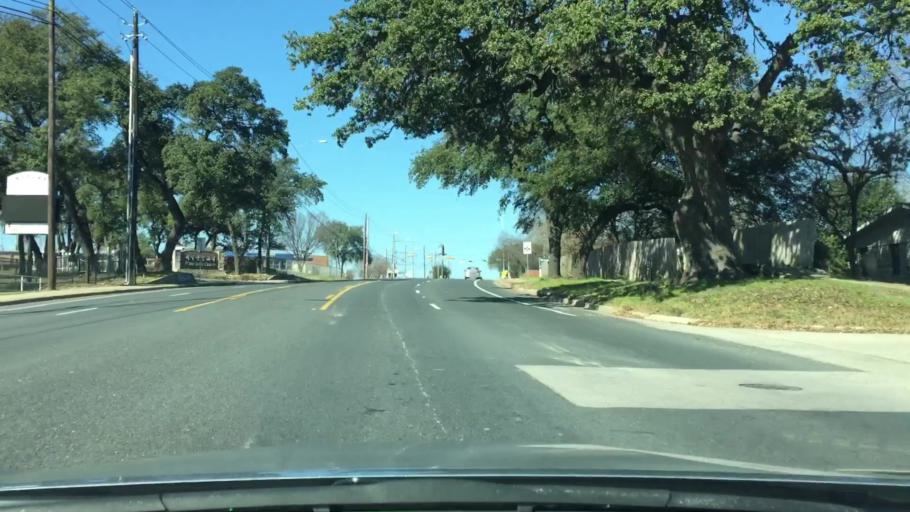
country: US
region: Texas
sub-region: Travis County
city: Wells Branch
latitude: 30.3792
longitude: -97.6818
